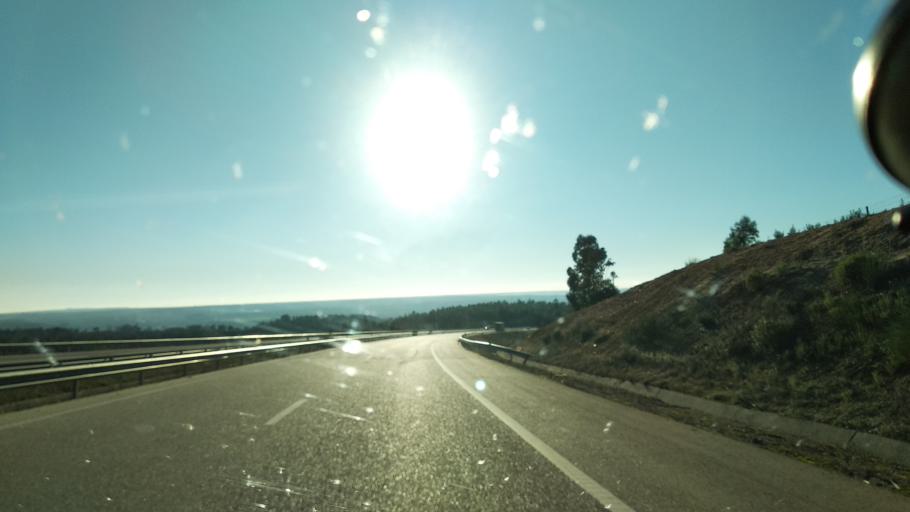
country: PT
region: Santarem
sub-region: Macao
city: Macao
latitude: 39.5034
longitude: -8.0258
